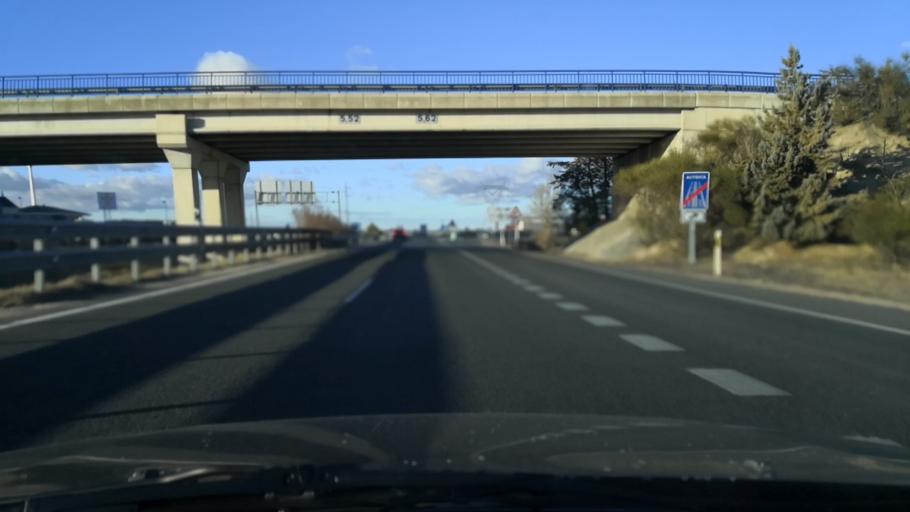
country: ES
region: Castille and Leon
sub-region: Provincia de Segovia
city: Martin Munoz de la Dehesa
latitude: 41.0499
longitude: -4.6999
